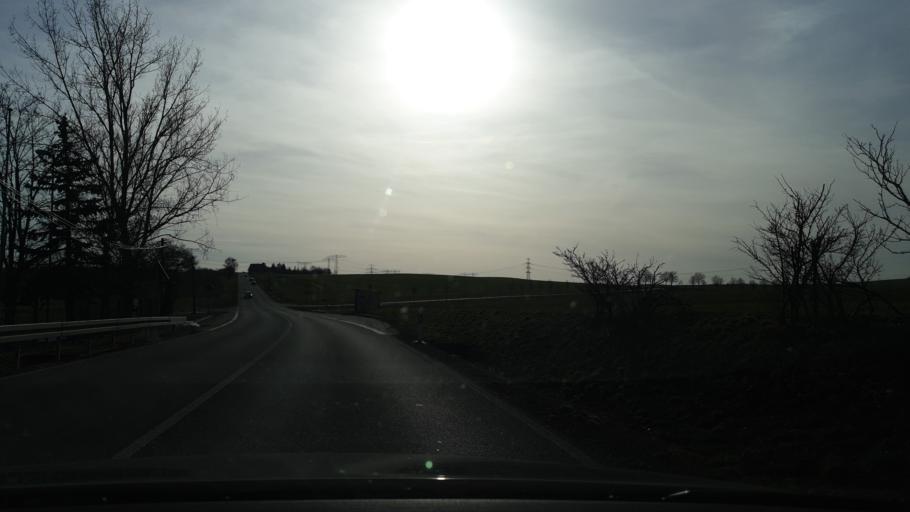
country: DE
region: Thuringia
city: Crimla
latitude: 50.8013
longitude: 12.0665
